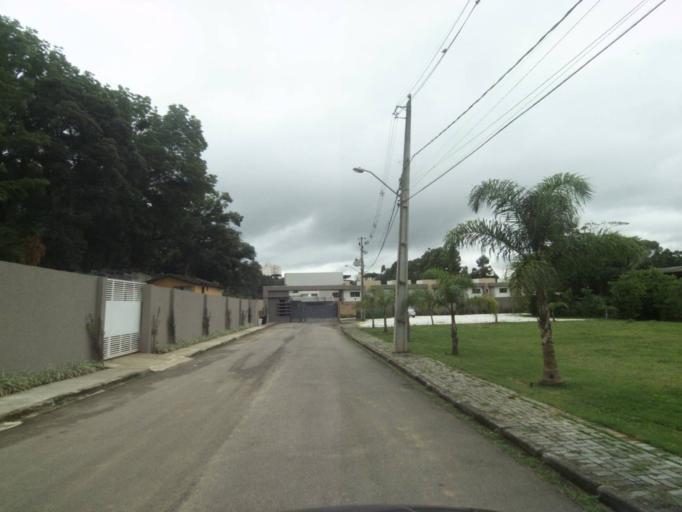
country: BR
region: Parana
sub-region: Curitiba
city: Curitiba
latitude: -25.4646
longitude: -49.3226
